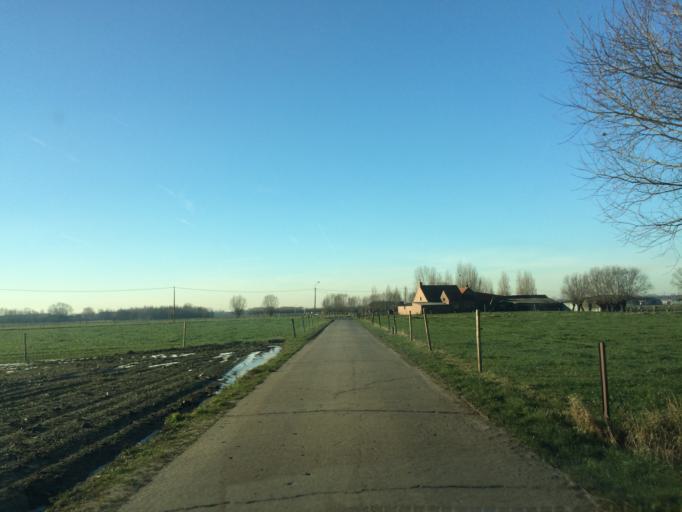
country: BE
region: Flanders
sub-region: Provincie West-Vlaanderen
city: Jabbeke
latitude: 51.1484
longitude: 3.0514
